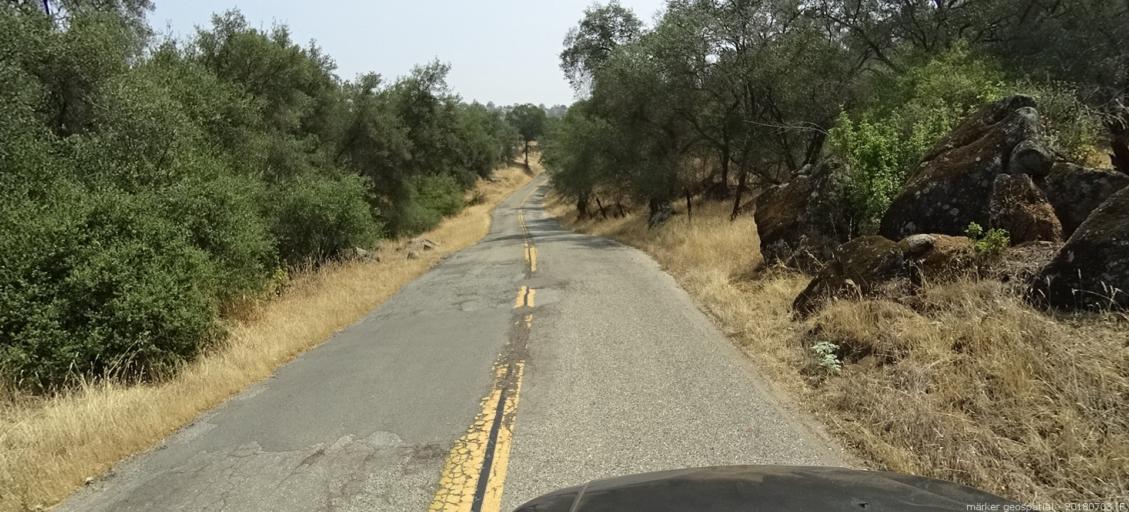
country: US
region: California
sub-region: Madera County
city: Yosemite Lakes
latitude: 37.0576
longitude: -119.6921
